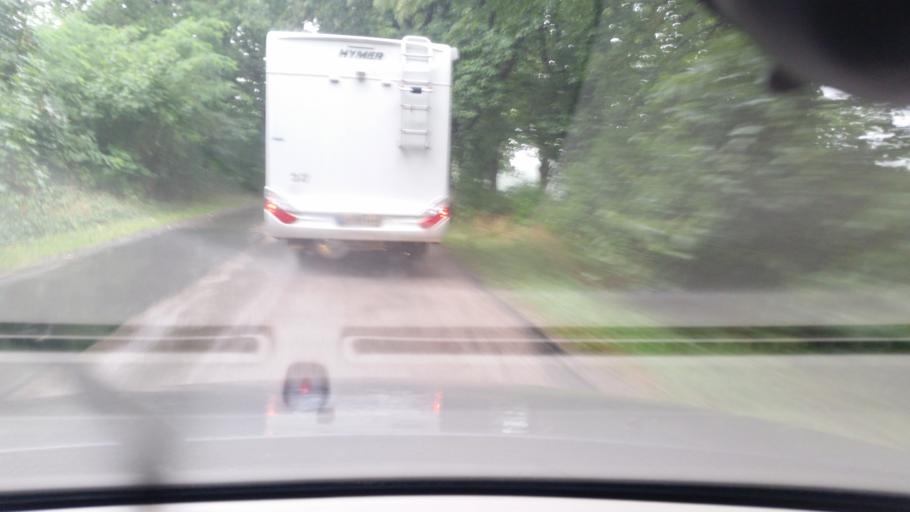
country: PL
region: Pomeranian Voivodeship
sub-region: Powiat wejherowski
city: Choczewo
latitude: 54.7455
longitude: 17.8066
